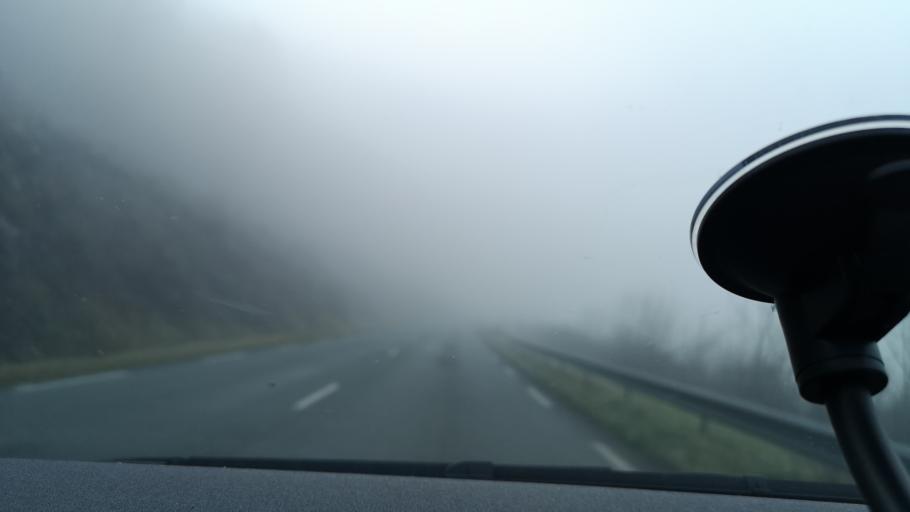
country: FR
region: Franche-Comte
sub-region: Departement du Doubs
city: Clerval
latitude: 47.4180
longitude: 6.5620
